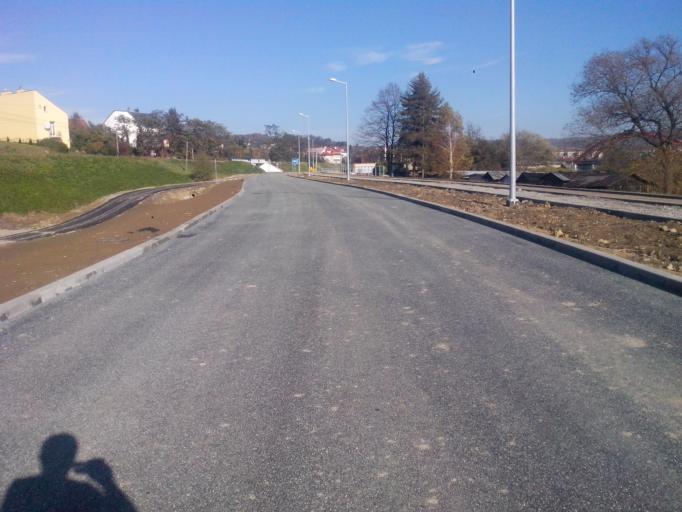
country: PL
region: Subcarpathian Voivodeship
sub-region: Powiat strzyzowski
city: Strzyzow
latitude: 49.8668
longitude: 21.7879
